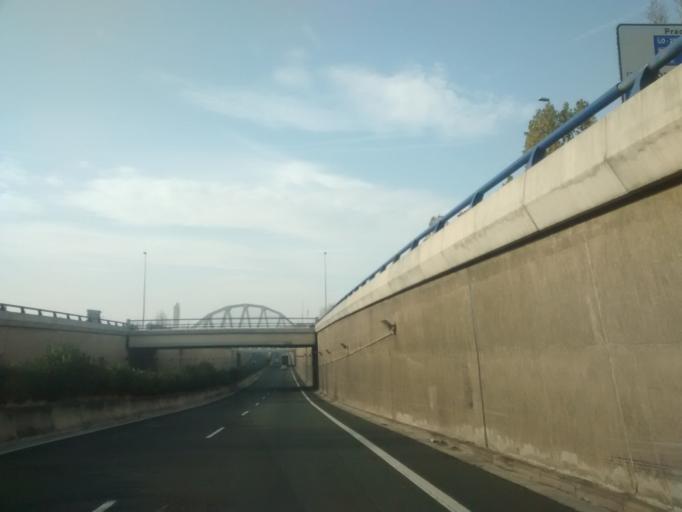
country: ES
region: La Rioja
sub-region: Provincia de La Rioja
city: Logrono
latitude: 42.4548
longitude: -2.4554
